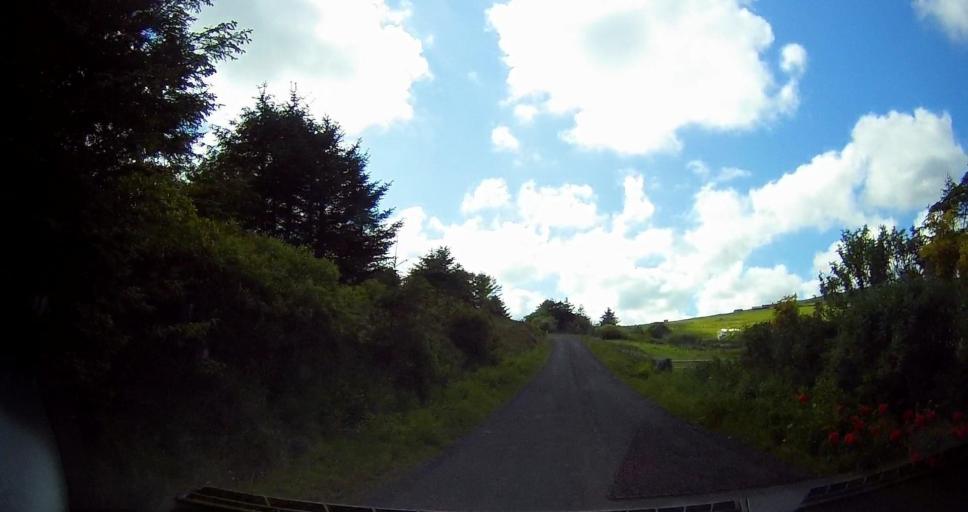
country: GB
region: Scotland
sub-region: Orkney Islands
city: Orkney
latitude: 59.0496
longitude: -3.1084
